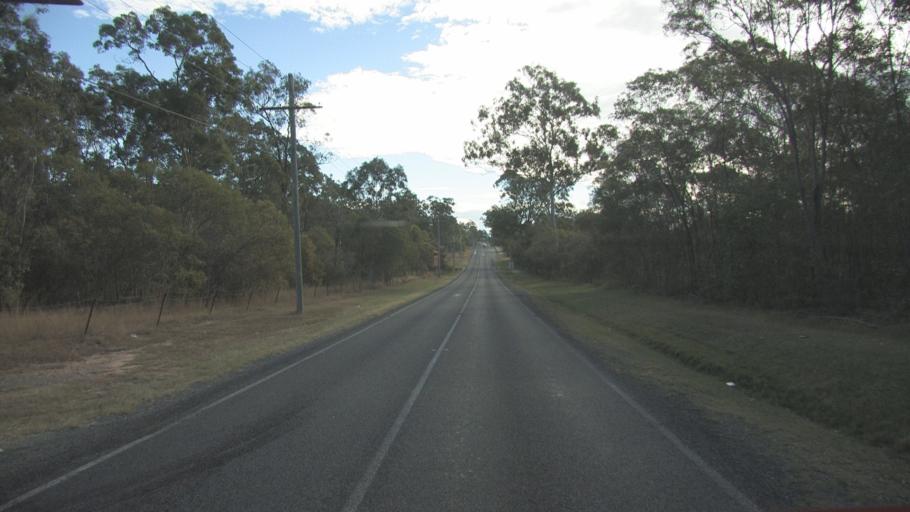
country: AU
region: Queensland
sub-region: Logan
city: Cedar Vale
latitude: -27.8351
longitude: 153.0407
